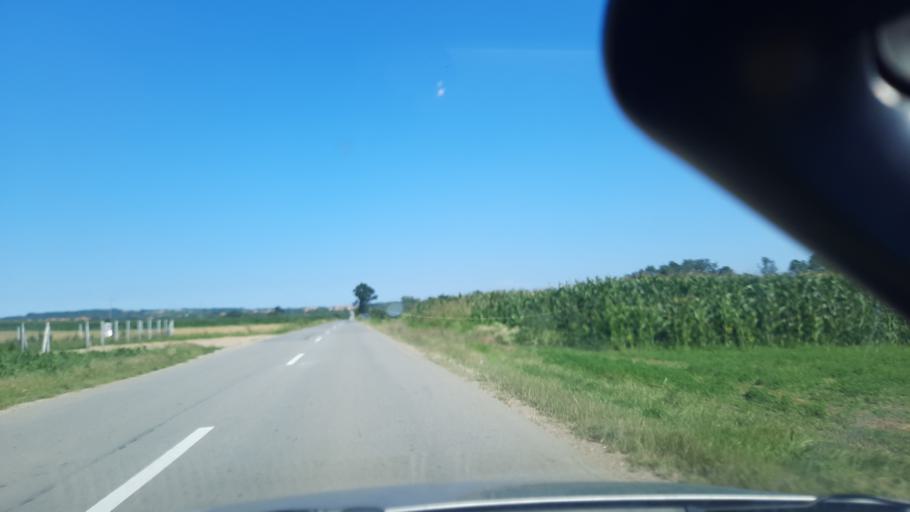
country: RS
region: Central Serbia
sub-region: Branicevski Okrug
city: Malo Crnice
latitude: 44.5776
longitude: 21.3351
